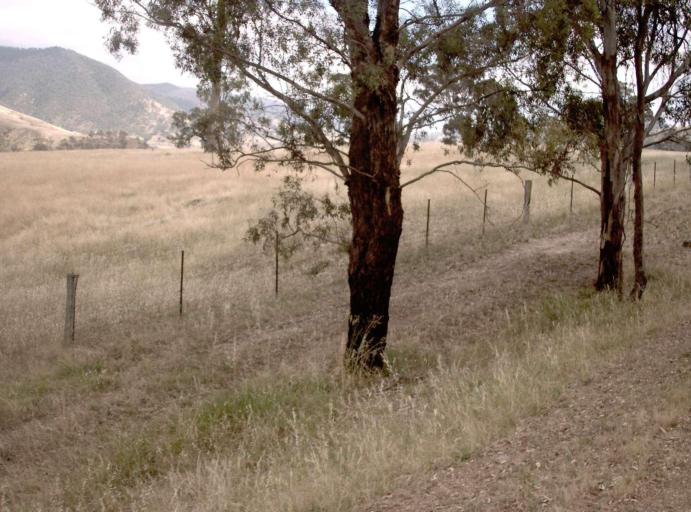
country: AU
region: Victoria
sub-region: Wellington
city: Heyfield
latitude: -37.6535
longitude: 146.6424
